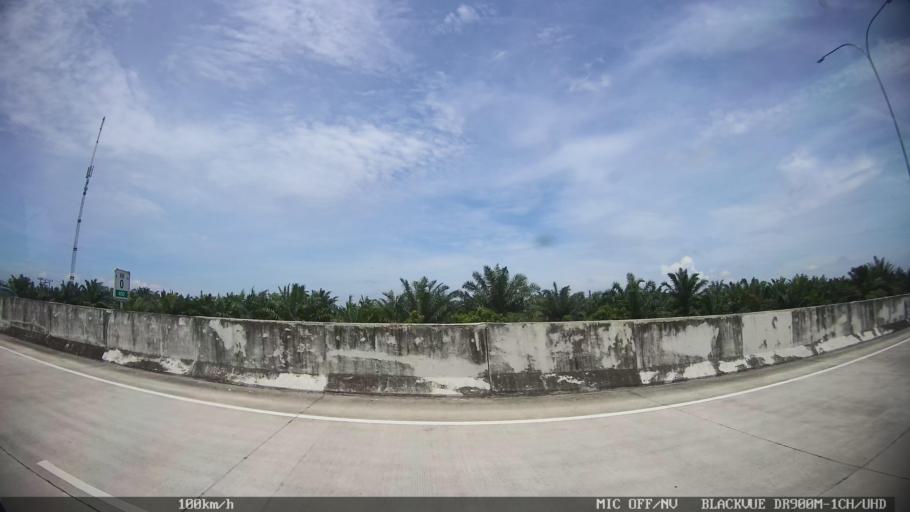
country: ID
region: North Sumatra
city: Percut
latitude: 3.5911
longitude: 98.8444
